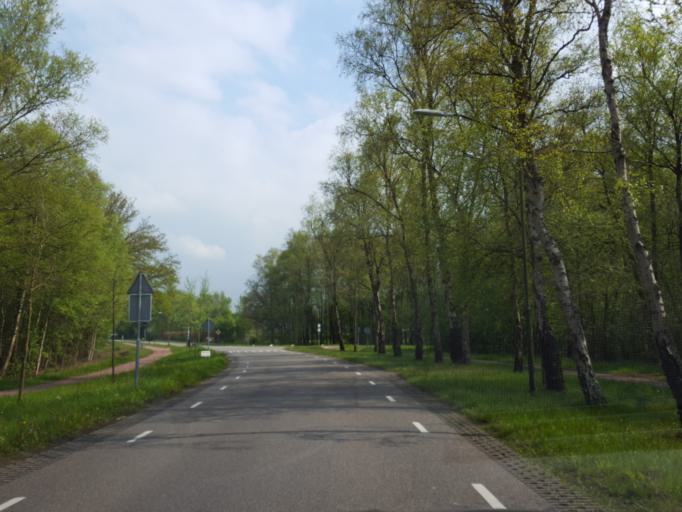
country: NL
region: North Brabant
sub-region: Gemeente Waalre
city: Waalre
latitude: 51.3830
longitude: 5.4165
